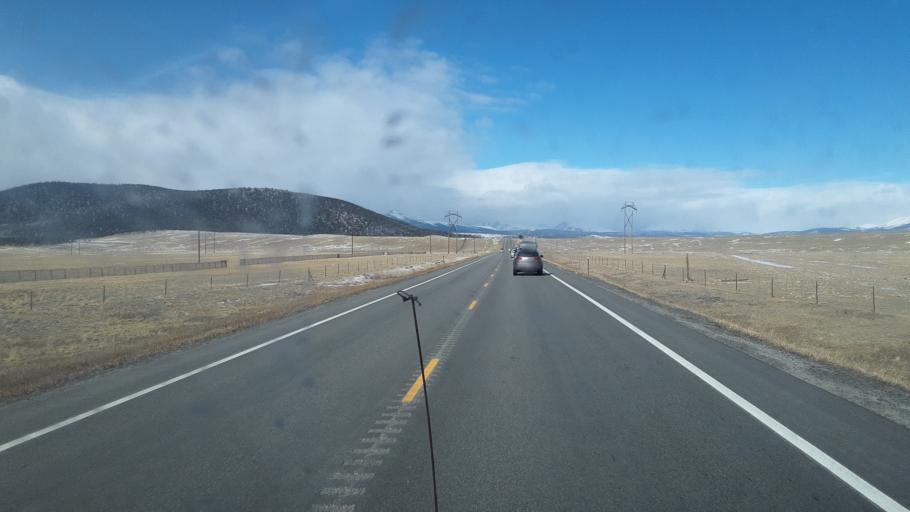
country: US
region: Colorado
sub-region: Park County
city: Fairplay
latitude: 39.0820
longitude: -105.9759
